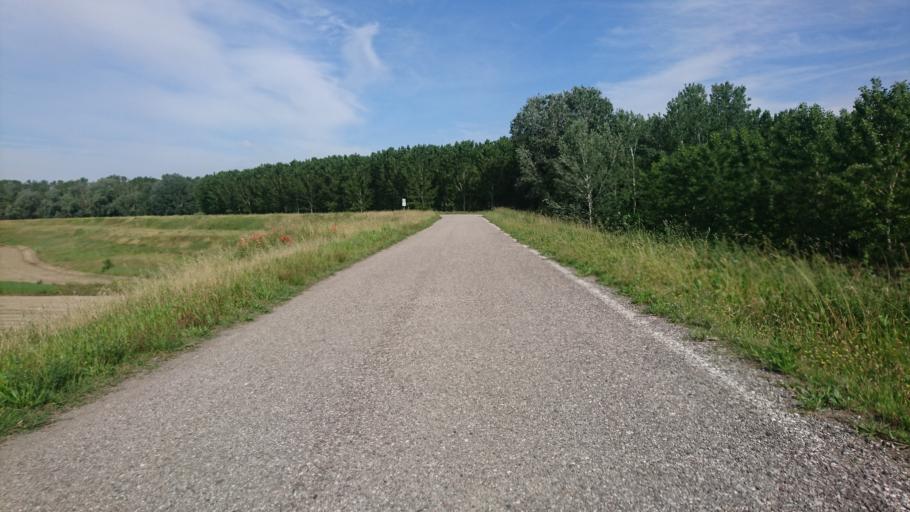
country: IT
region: Veneto
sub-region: Provincia di Rovigo
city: Bergantino
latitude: 45.0503
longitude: 11.2612
